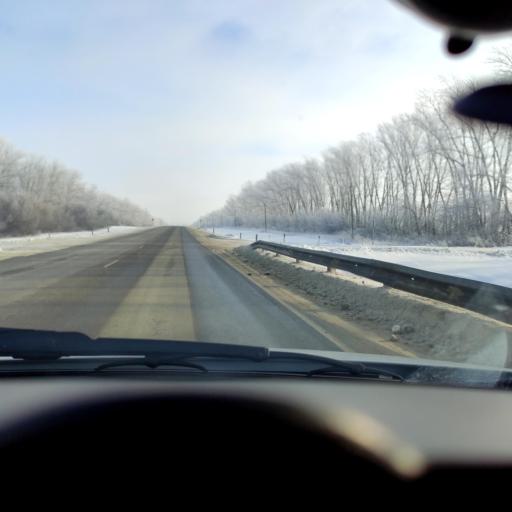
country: RU
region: Belgorod
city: Troitskiy
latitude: 51.6185
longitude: 37.5416
